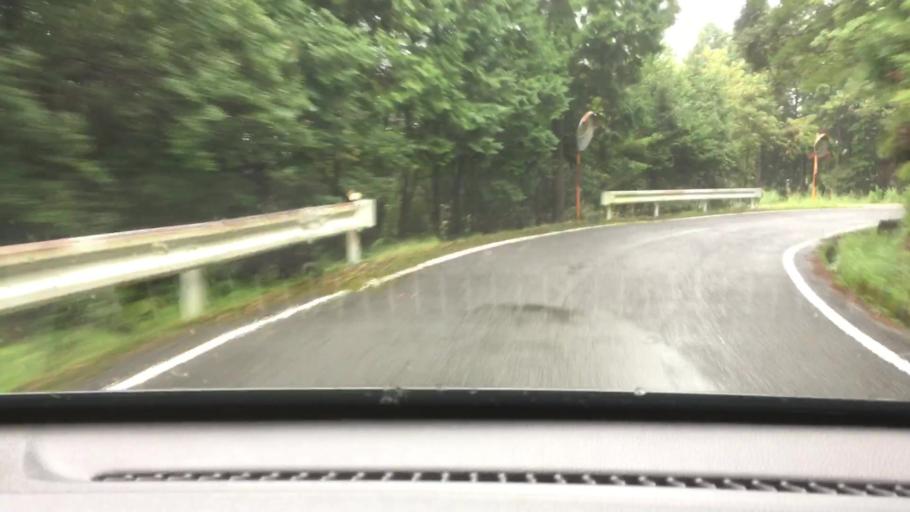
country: JP
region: Nagasaki
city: Togitsu
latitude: 32.9200
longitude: 129.7270
